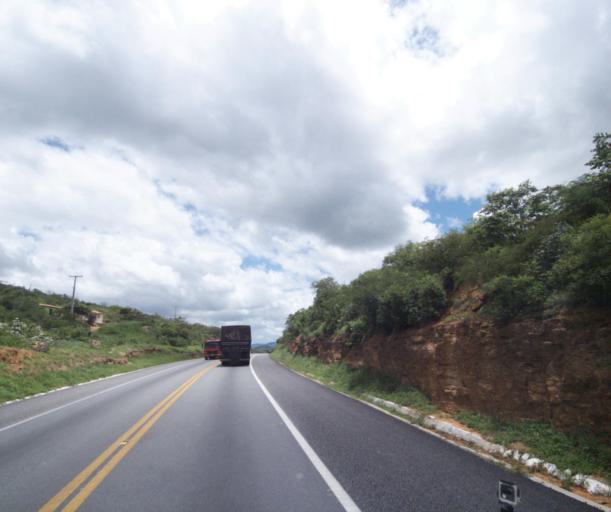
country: BR
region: Bahia
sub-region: Pocoes
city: Pocoes
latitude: -14.3664
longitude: -40.3447
